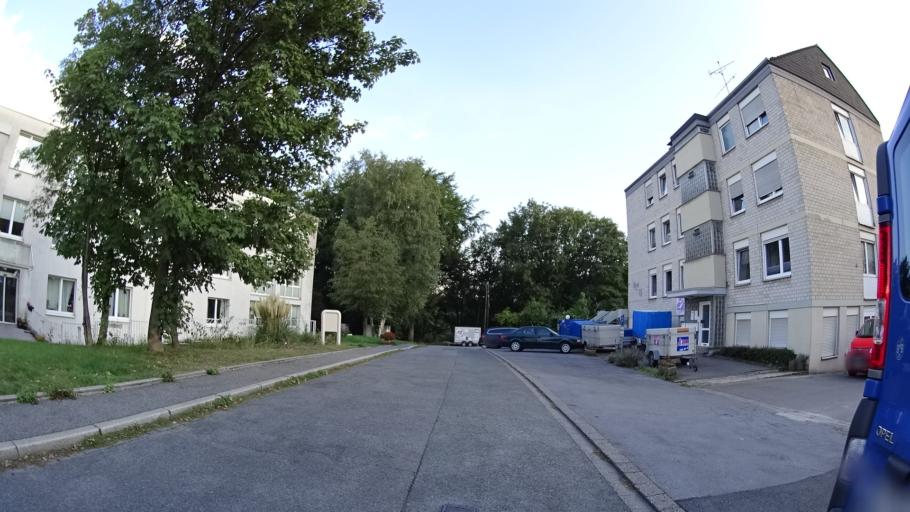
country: DE
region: North Rhine-Westphalia
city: Witten
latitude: 51.4351
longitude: 7.3524
